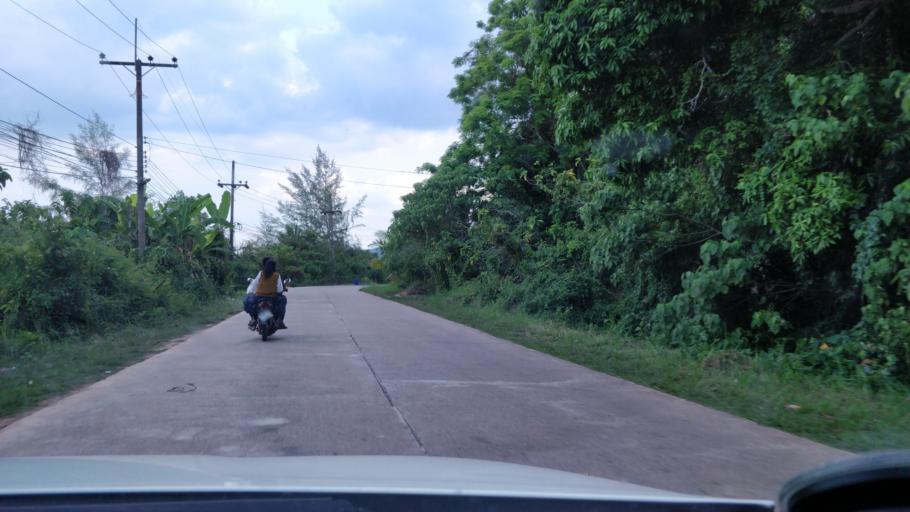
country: TH
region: Krabi
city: Ko Lanta
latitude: 7.5766
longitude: 99.0687
